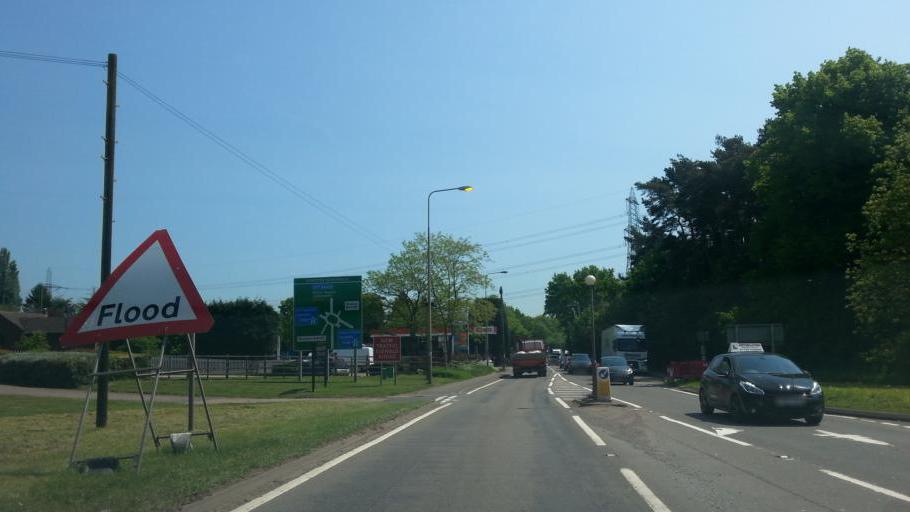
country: GB
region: England
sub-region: Leicestershire
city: Hinckley
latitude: 52.5175
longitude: -1.3670
